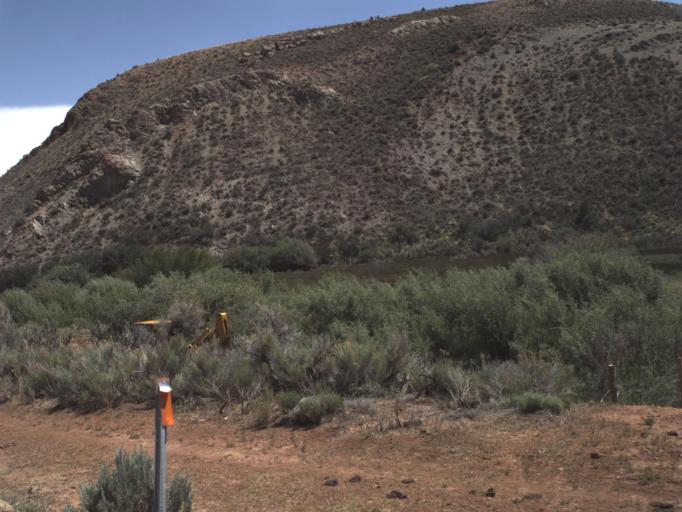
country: US
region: Utah
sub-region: Rich County
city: Randolph
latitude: 41.5039
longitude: -111.2912
